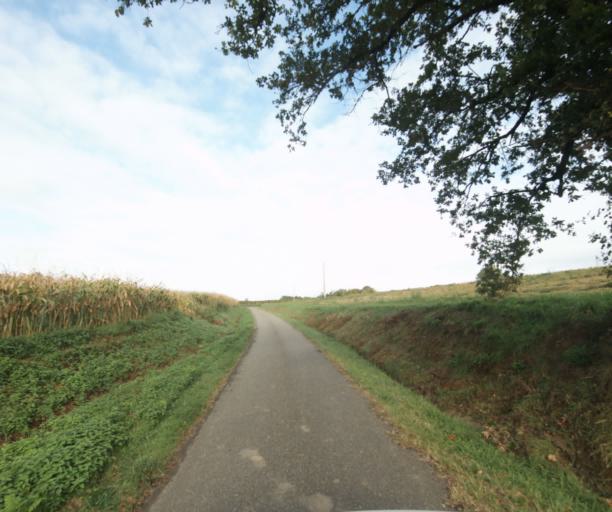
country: FR
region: Midi-Pyrenees
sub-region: Departement du Gers
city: Nogaro
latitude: 43.8086
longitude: -0.0540
